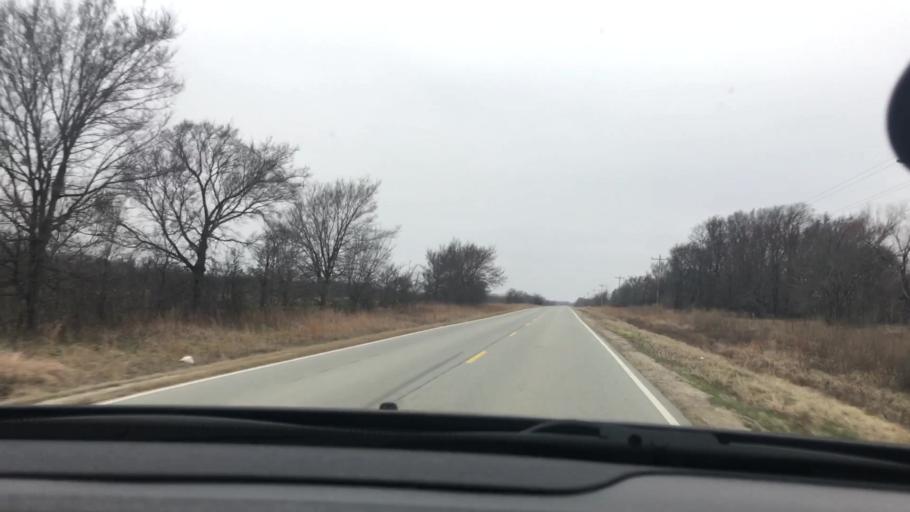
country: US
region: Oklahoma
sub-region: Coal County
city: Coalgate
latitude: 34.5266
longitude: -96.2682
